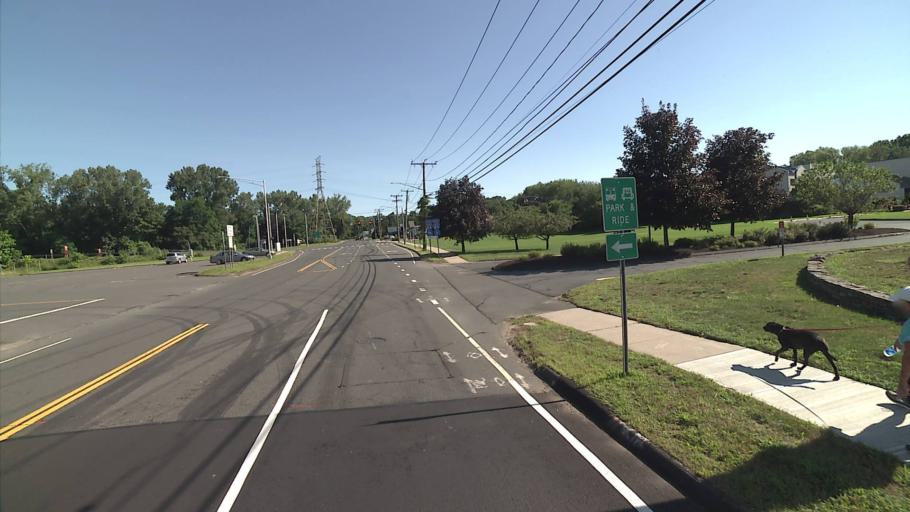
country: US
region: Connecticut
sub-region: New Haven County
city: Cheshire Village
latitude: 41.5726
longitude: -72.8959
